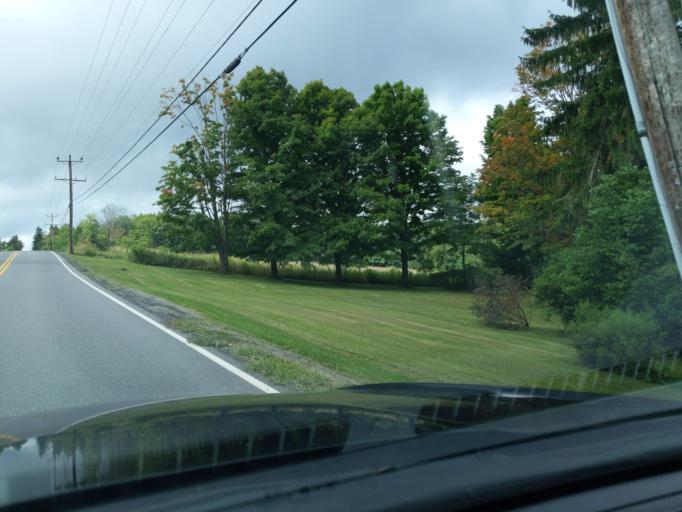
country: US
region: Pennsylvania
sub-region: Blair County
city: Claysburg
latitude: 40.3274
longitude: -78.5648
